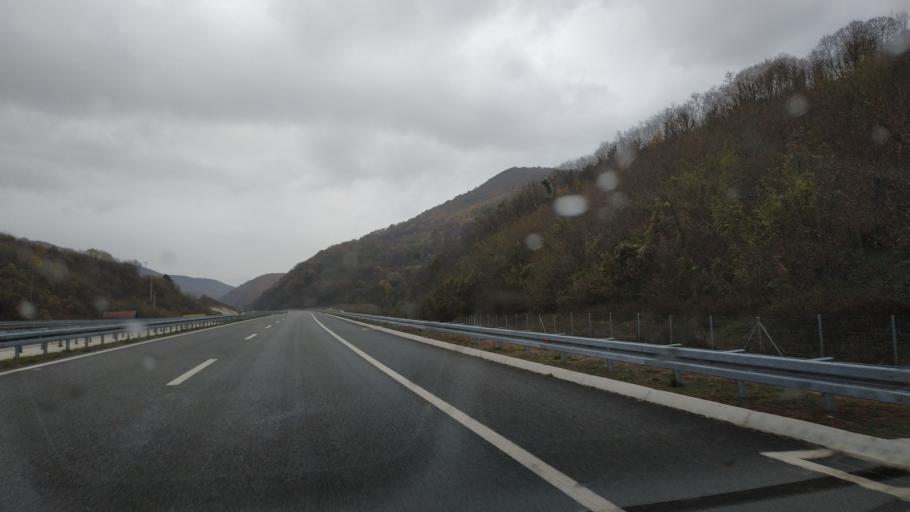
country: RS
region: Central Serbia
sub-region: Nisavski Okrug
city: Niska Banja
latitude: 43.3003
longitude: 22.0611
